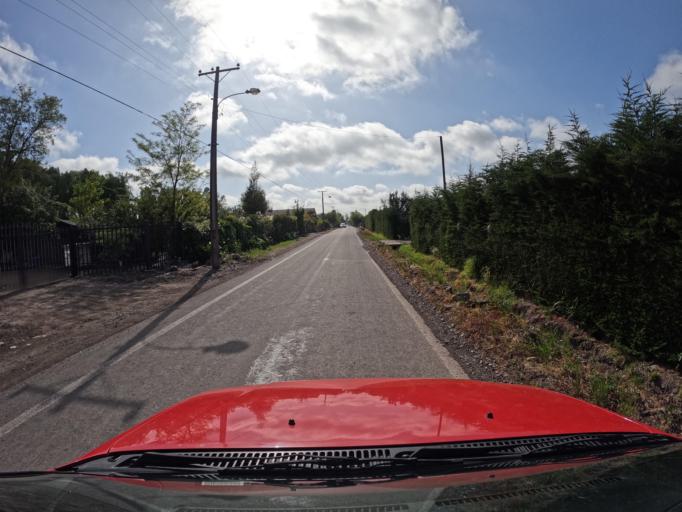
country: CL
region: Maule
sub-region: Provincia de Curico
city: Rauco
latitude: -34.8873
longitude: -71.2636
